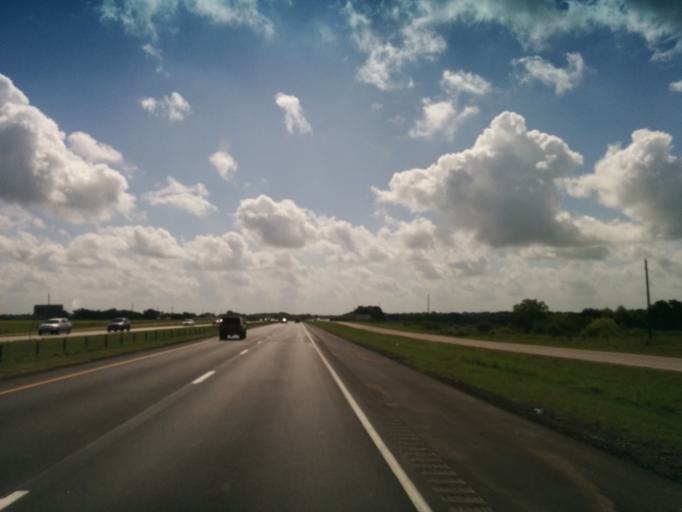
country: US
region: Texas
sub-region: Colorado County
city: Weimar
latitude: 29.6922
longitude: -96.7420
